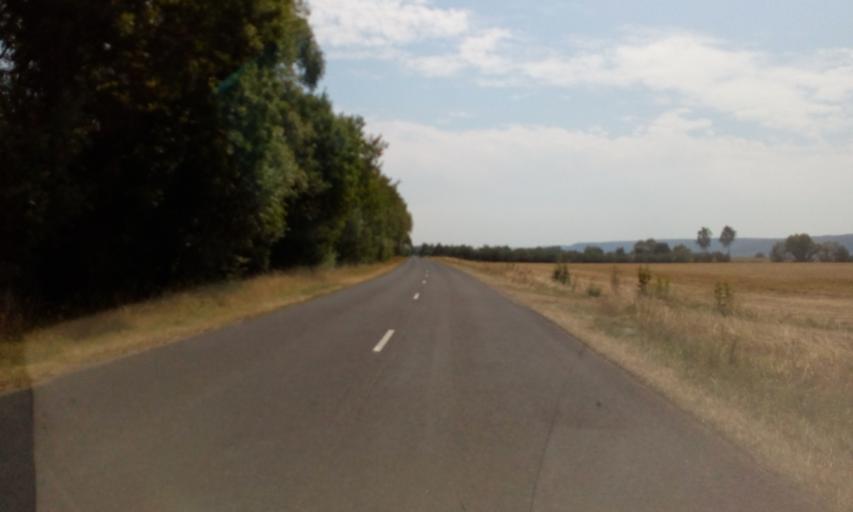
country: FR
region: Lorraine
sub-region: Departement de la Meuse
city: Vigneulles-les-Hattonchatel
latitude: 49.0834
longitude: 5.6349
